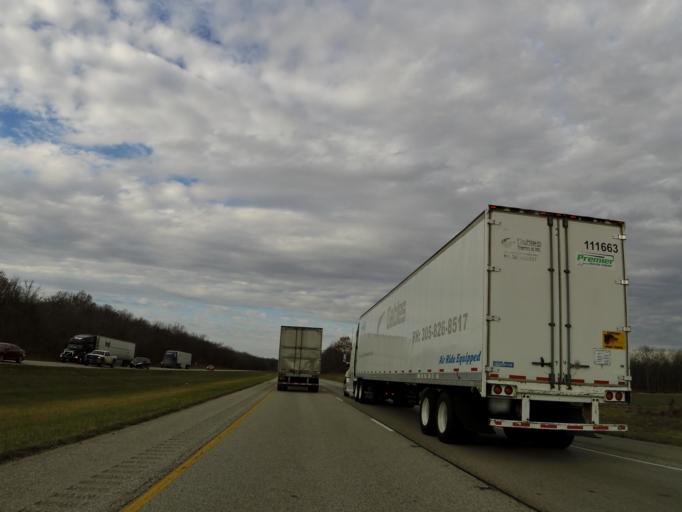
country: US
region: Illinois
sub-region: Washington County
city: Nashville
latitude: 38.3913
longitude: -89.2957
